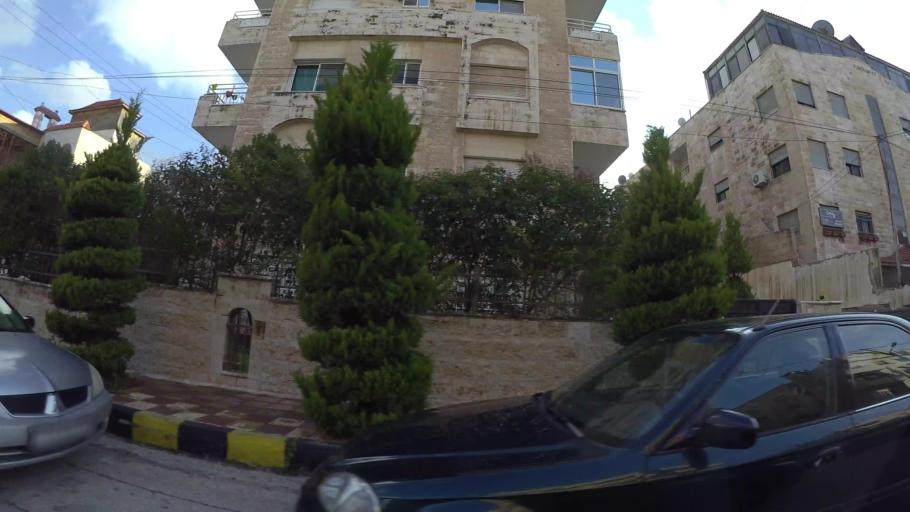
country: JO
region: Amman
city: Al Jubayhah
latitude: 31.9825
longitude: 35.8850
